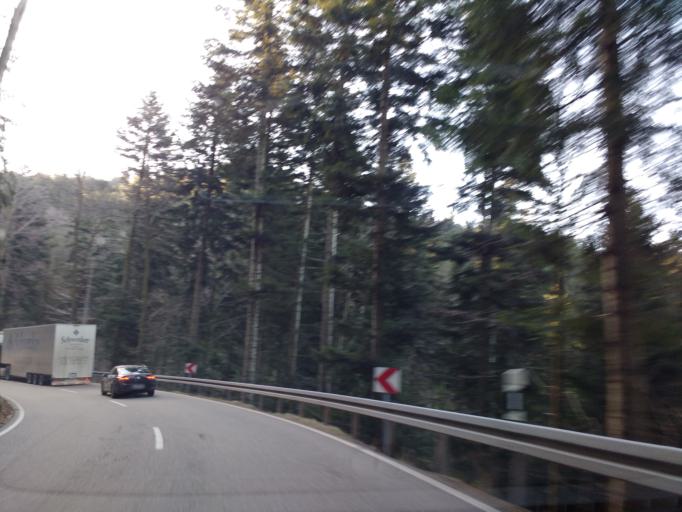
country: DE
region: Baden-Wuerttemberg
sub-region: Freiburg Region
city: Bad Peterstal-Griesbach
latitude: 48.4501
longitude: 8.2539
